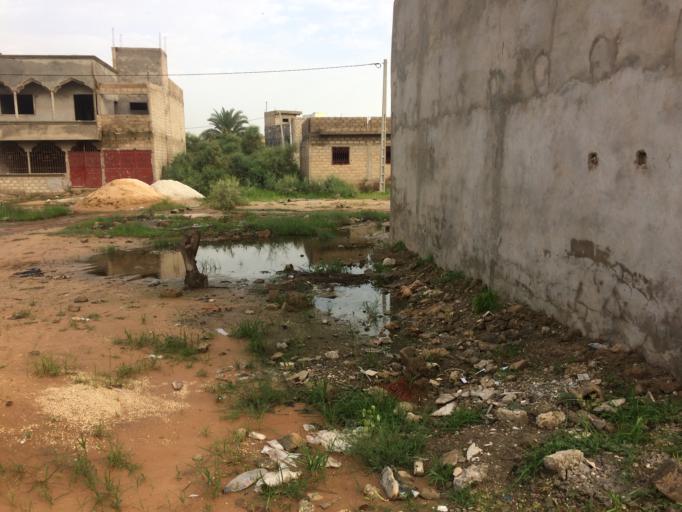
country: SN
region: Dakar
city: Pikine
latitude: 14.7416
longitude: -17.3051
